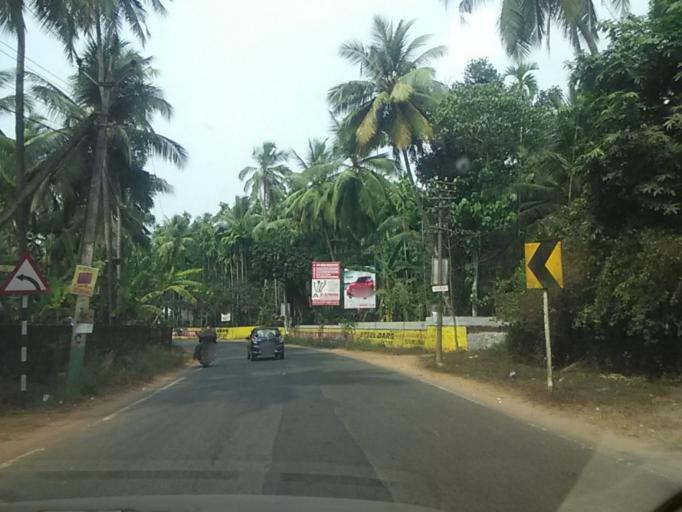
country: IN
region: Kerala
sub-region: Kozhikode
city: Naduvannur
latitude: 11.4720
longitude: 75.7741
